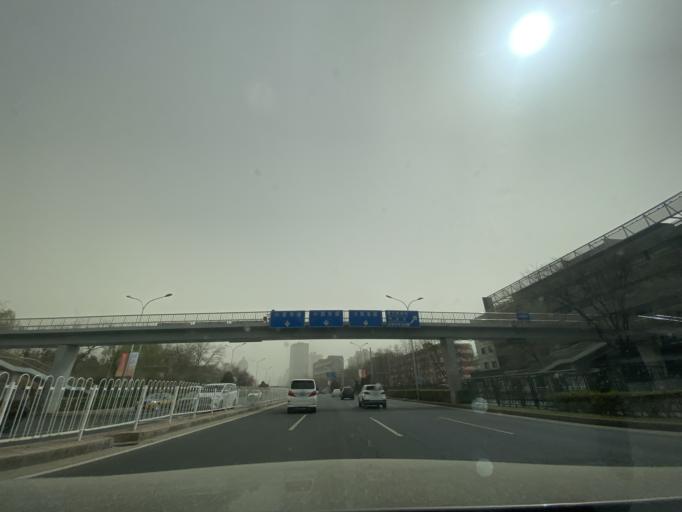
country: CN
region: Beijing
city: Sijiqing
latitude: 39.9383
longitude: 116.3109
